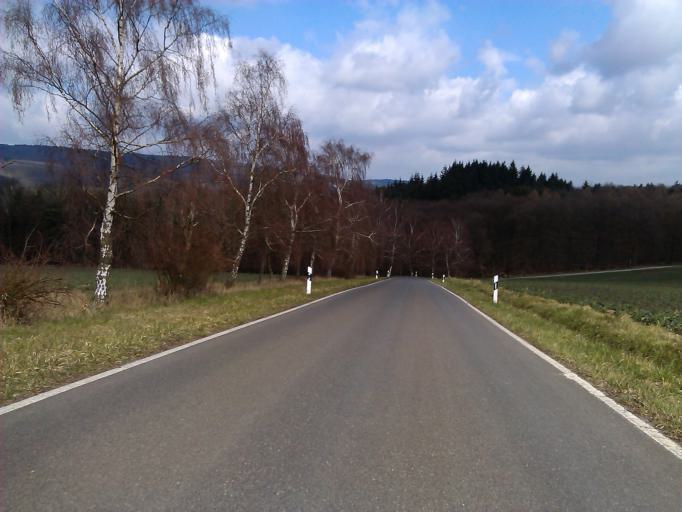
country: DE
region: Rheinland-Pfalz
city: Bingen am Rhein
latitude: 49.9866
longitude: 7.8838
